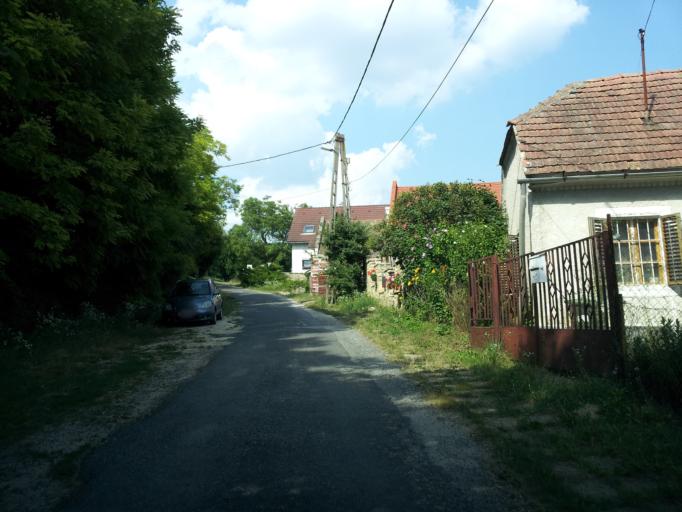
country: HU
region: Veszprem
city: Balatonfured
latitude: 46.9995
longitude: 17.8308
